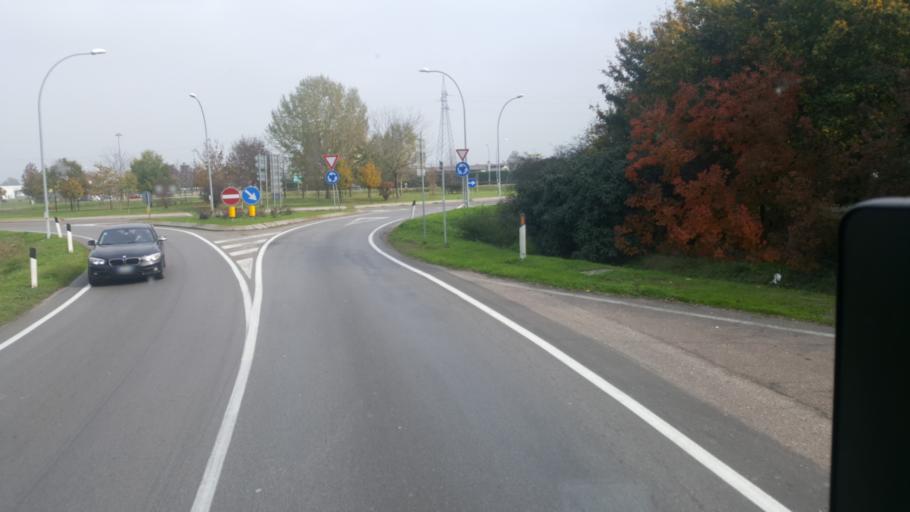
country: IT
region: Lombardy
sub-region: Provincia di Mantova
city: Pegognaga
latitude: 44.9874
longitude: 10.8441
